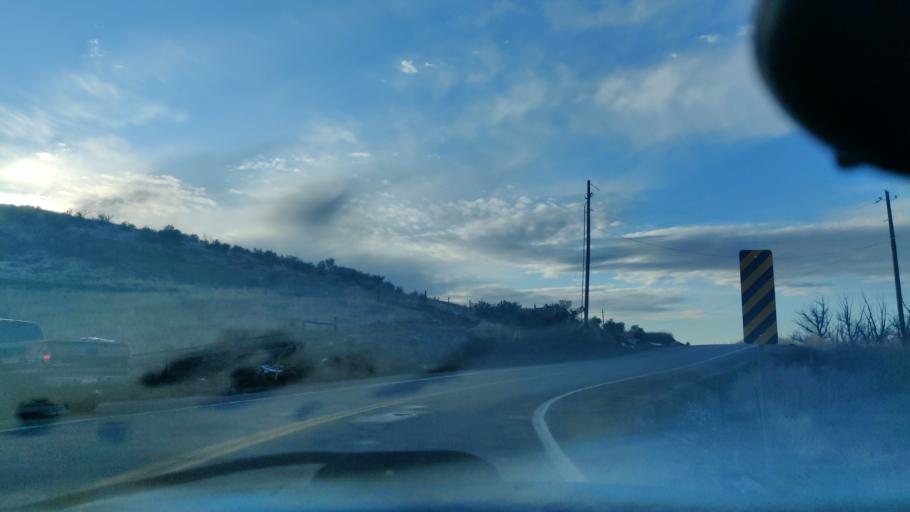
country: US
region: Idaho
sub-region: Ada County
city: Eagle
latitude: 43.7307
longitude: -116.2734
